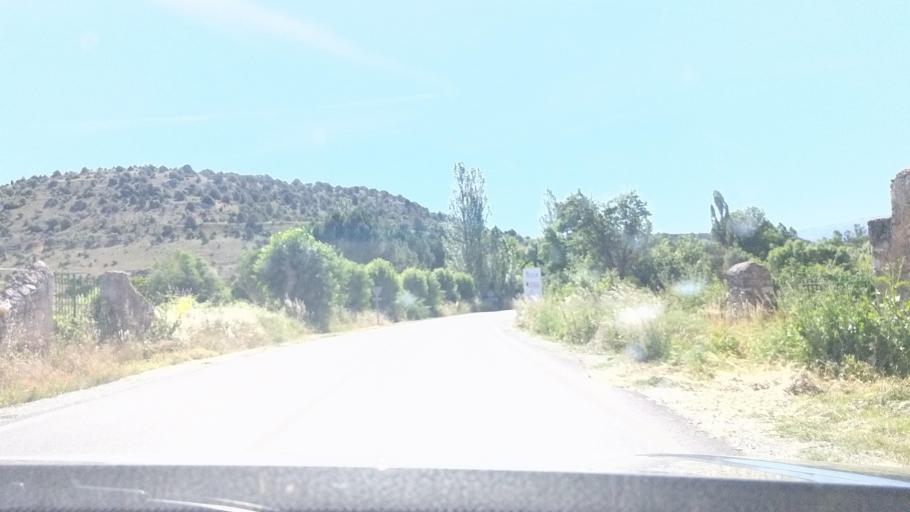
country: ES
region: Castille and Leon
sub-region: Provincia de Segovia
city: Pedraza
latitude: 41.1422
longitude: -3.8249
